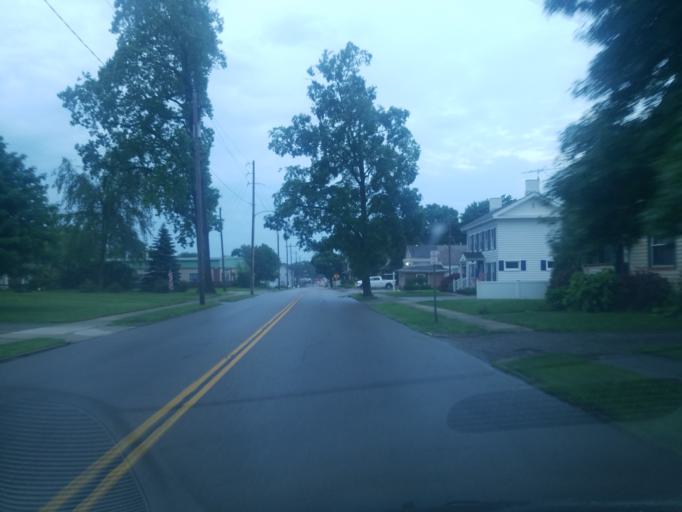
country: US
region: Ohio
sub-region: Columbiana County
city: Salem
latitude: 40.9048
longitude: -80.8520
